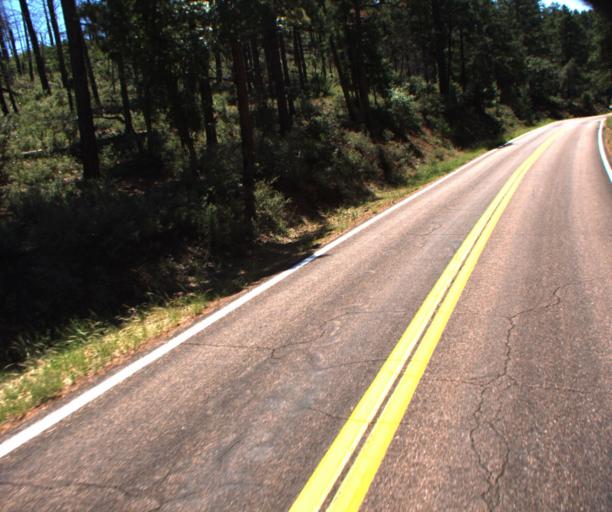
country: US
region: Arizona
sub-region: Greenlee County
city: Morenci
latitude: 33.5382
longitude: -109.3096
